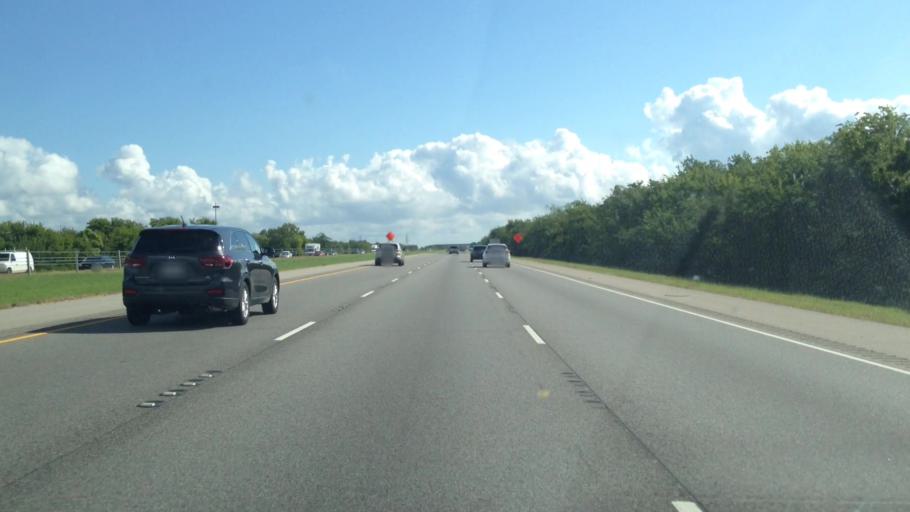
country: US
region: Louisiana
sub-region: Saint Tammany Parish
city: Eden Isle
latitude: 30.1386
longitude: -89.8682
